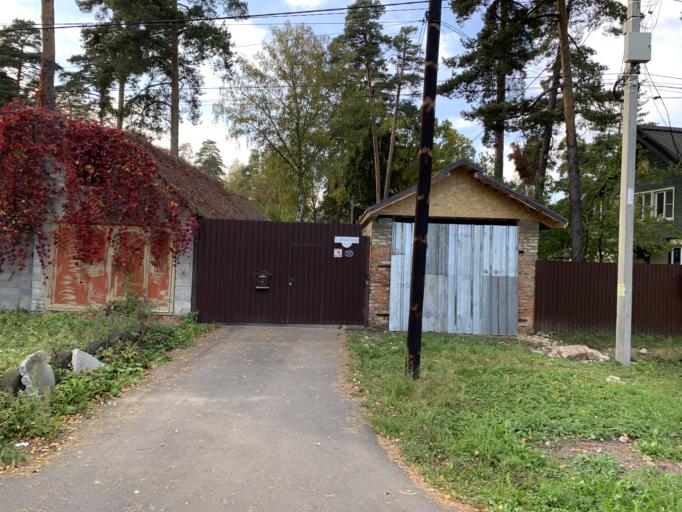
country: RU
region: Moskovskaya
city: Mamontovka
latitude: 55.9817
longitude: 37.8314
